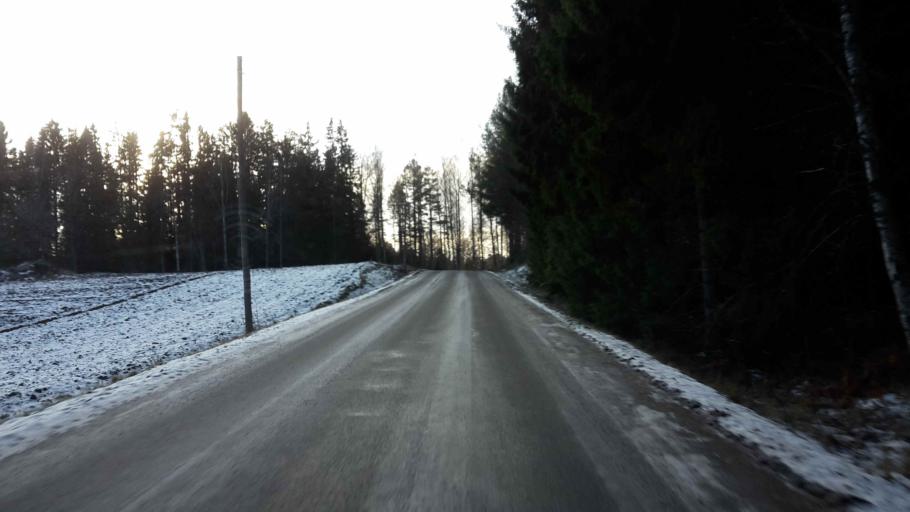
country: SE
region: OEstergoetland
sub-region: Atvidabergs Kommun
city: Atvidaberg
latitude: 58.2654
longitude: 16.1414
